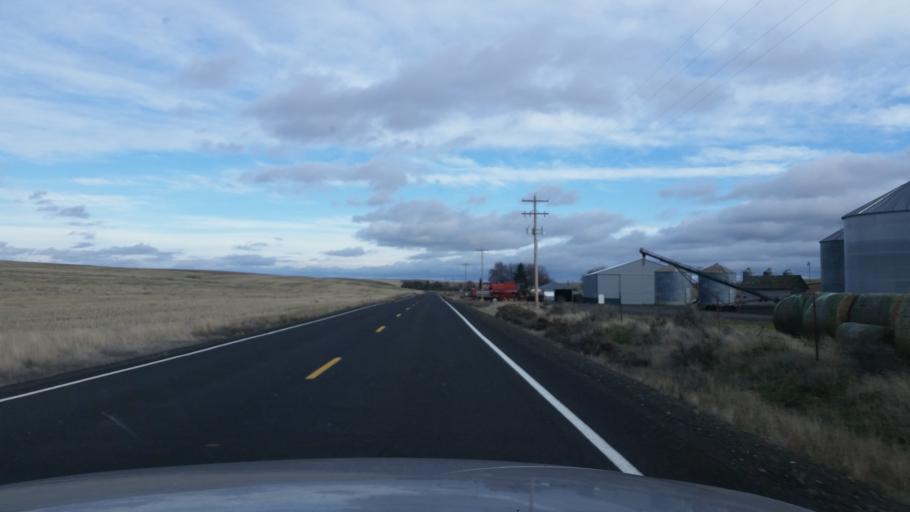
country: US
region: Washington
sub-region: Lincoln County
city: Davenport
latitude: 47.3521
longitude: -118.0670
